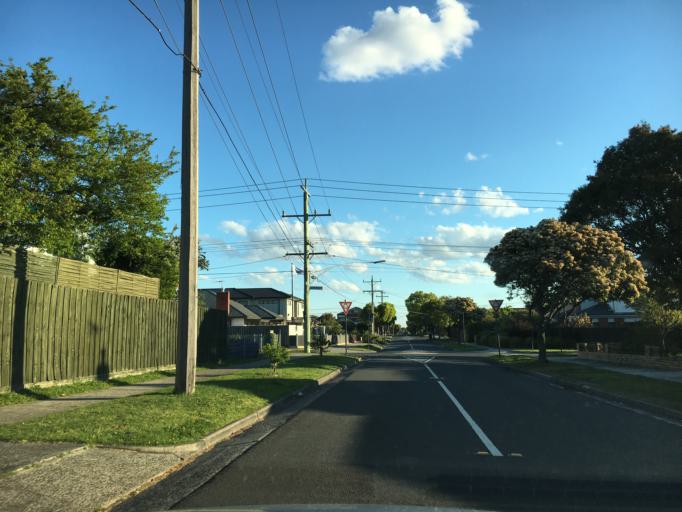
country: AU
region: Victoria
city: Clayton
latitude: -37.9057
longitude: 145.1077
